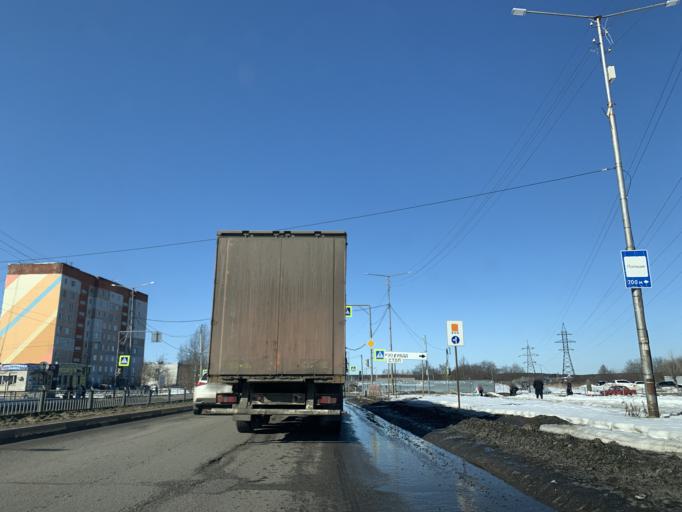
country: RU
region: Jaroslavl
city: Tutayev
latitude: 57.8653
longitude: 39.5089
